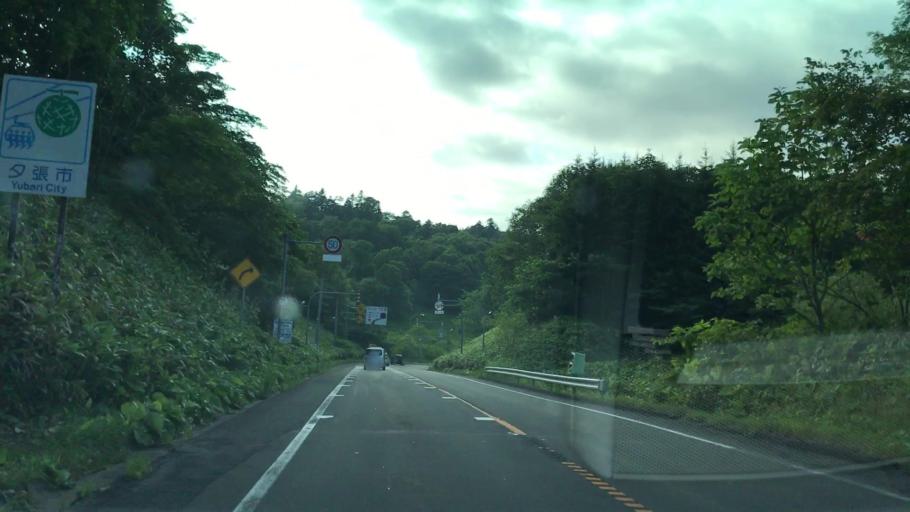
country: JP
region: Hokkaido
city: Iwamizawa
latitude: 42.9183
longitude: 142.1187
